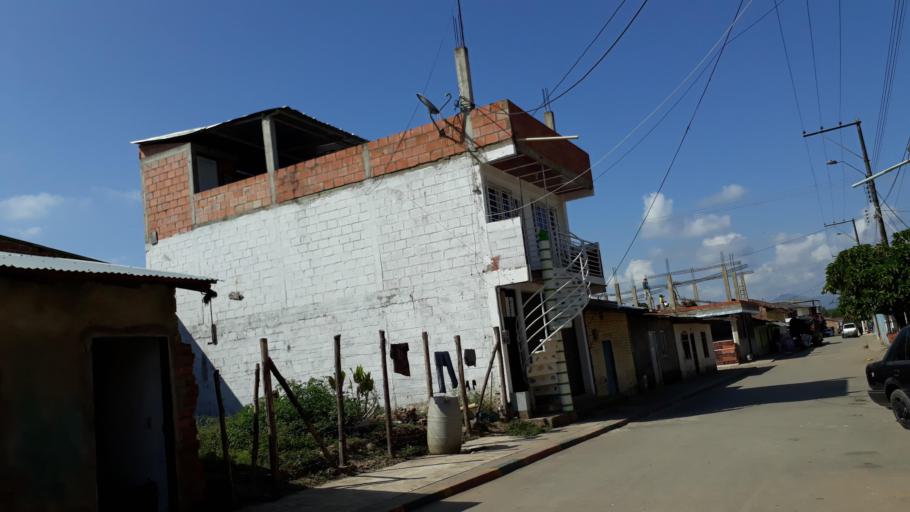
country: CO
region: Cauca
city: Buenos Aires
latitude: 3.1232
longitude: -76.6226
